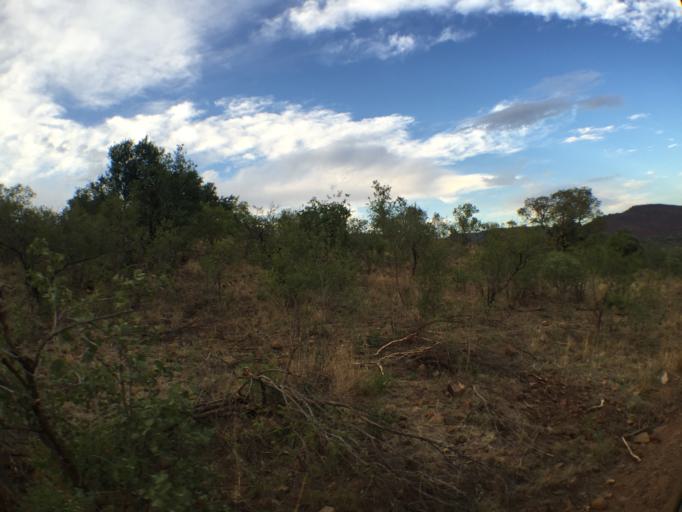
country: ZA
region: North-West
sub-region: Bojanala Platinum District Municipality
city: Mogwase
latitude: -25.2232
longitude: 27.0679
